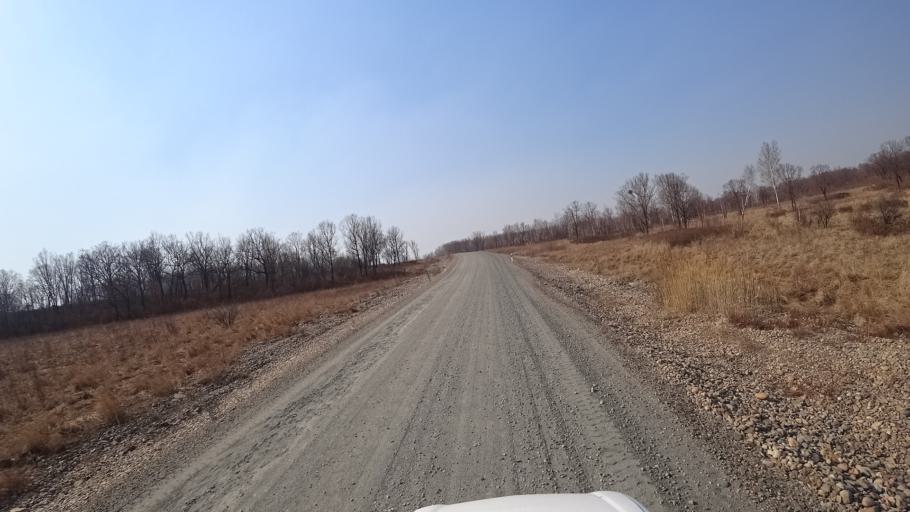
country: RU
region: Amur
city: Novobureyskiy
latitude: 49.8258
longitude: 129.9942
